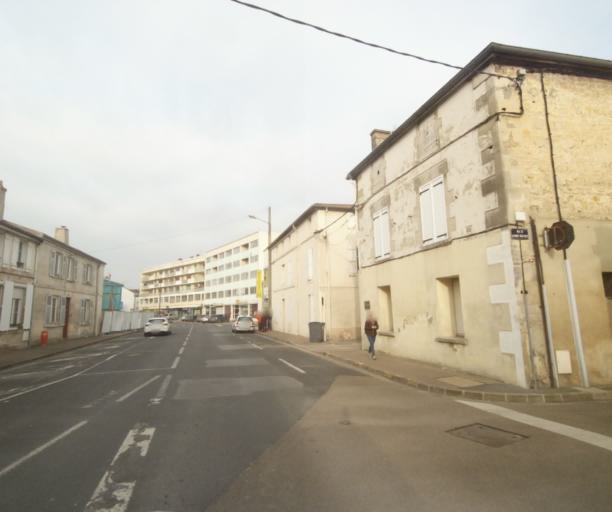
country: FR
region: Champagne-Ardenne
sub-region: Departement de la Haute-Marne
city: Saint-Dizier
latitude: 48.6378
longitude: 4.9529
